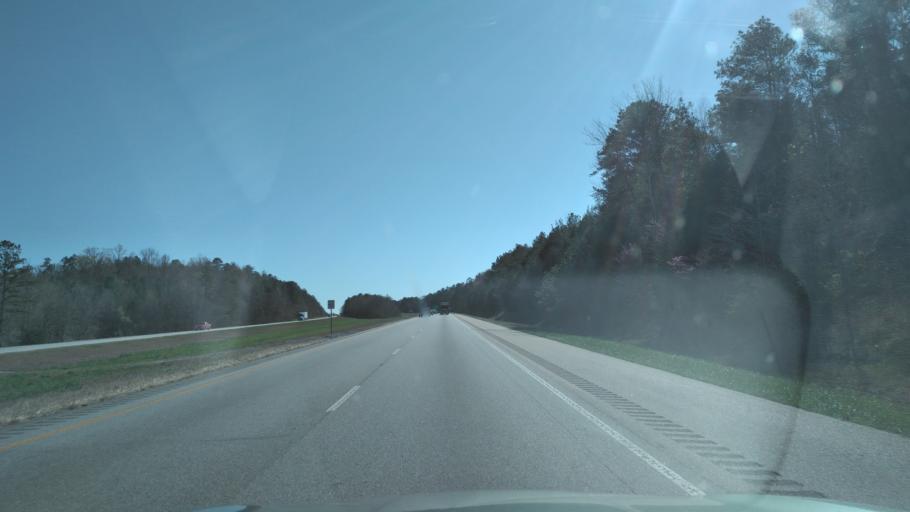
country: US
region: Alabama
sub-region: Lowndes County
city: Fort Deposit
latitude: 32.0092
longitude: -86.5218
